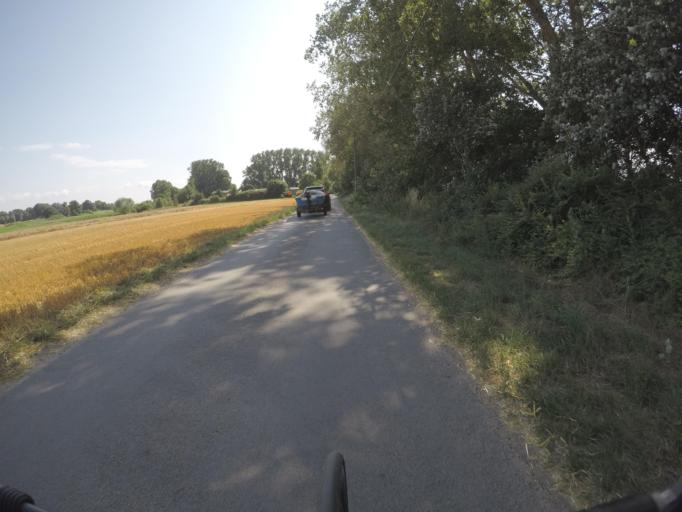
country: DE
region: Mecklenburg-Vorpommern
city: Gingst
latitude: 54.4363
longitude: 13.1749
